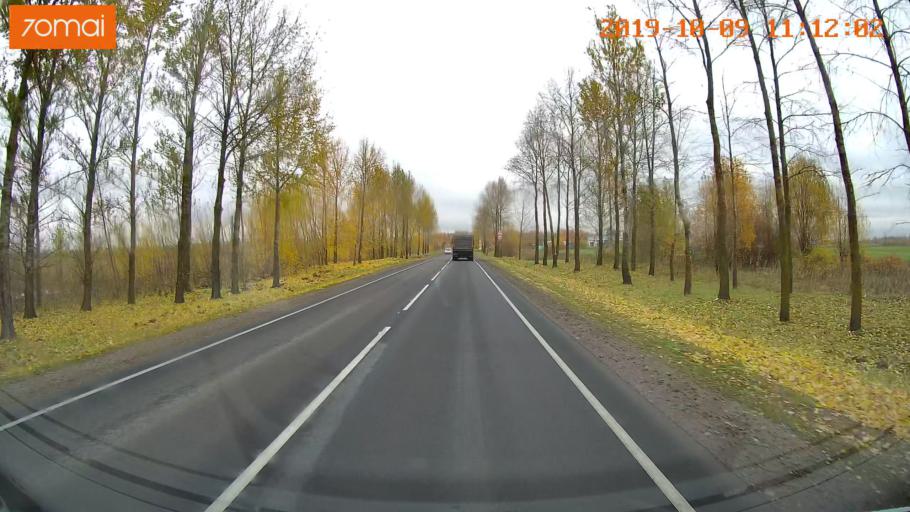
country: RU
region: Vologda
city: Vologda
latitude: 59.1739
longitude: 39.8261
